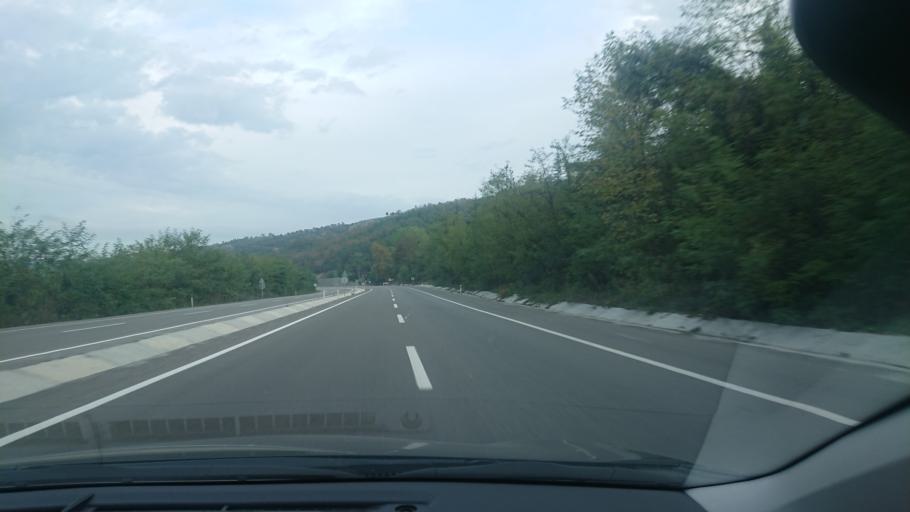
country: TR
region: Zonguldak
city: Beycuma
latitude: 41.3293
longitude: 32.0448
